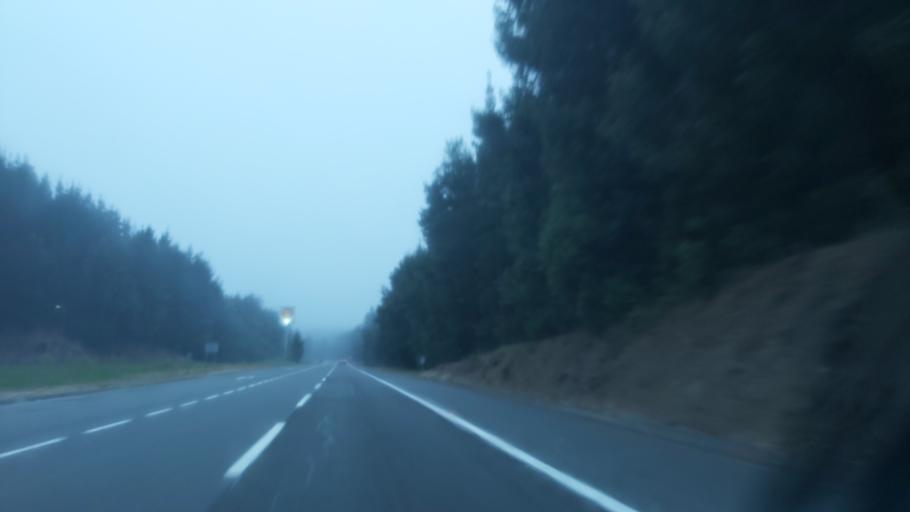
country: CL
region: Biobio
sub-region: Provincia de Concepcion
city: Penco
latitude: -36.7475
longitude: -72.9202
